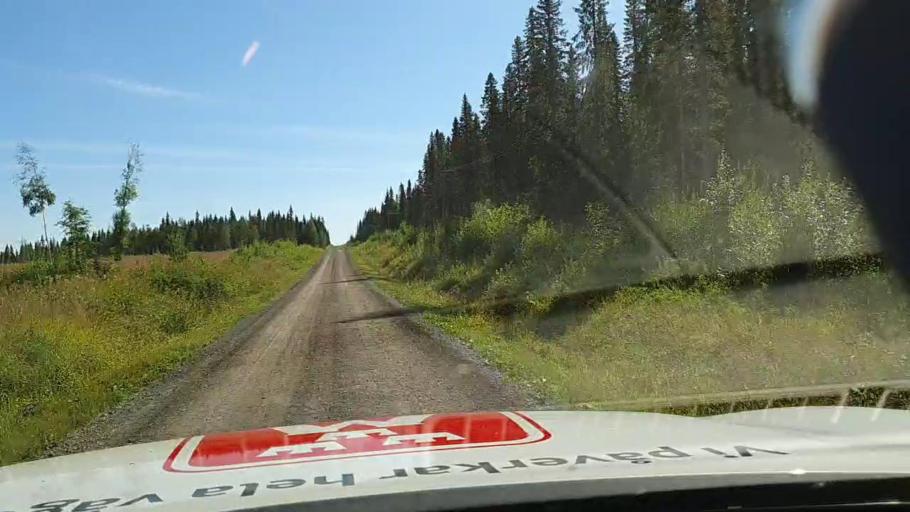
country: SE
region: Jaemtland
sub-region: Stroemsunds Kommun
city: Stroemsund
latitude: 63.7838
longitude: 15.3054
